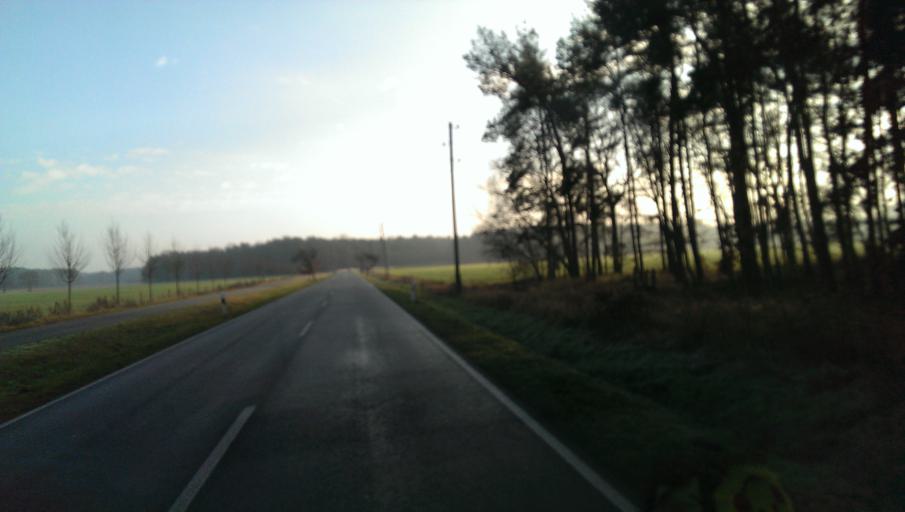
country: DE
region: Brandenburg
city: Schilda
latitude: 51.5991
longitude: 13.3506
